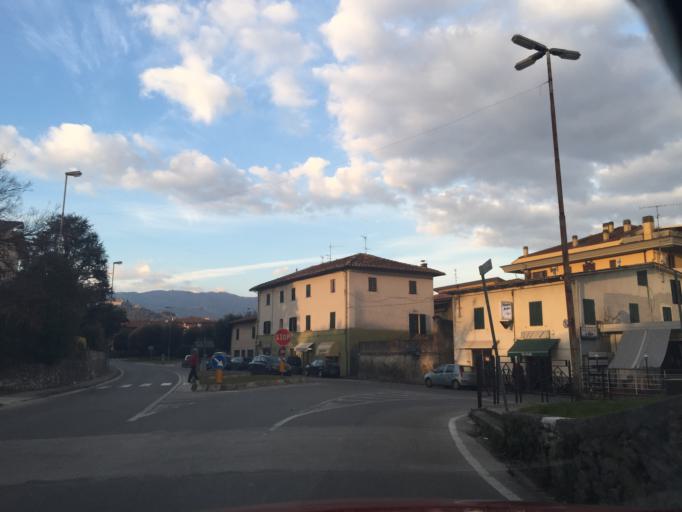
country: IT
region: Tuscany
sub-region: Provincia di Pistoia
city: Borgo a Buggiano
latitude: 43.8742
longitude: 10.7321
